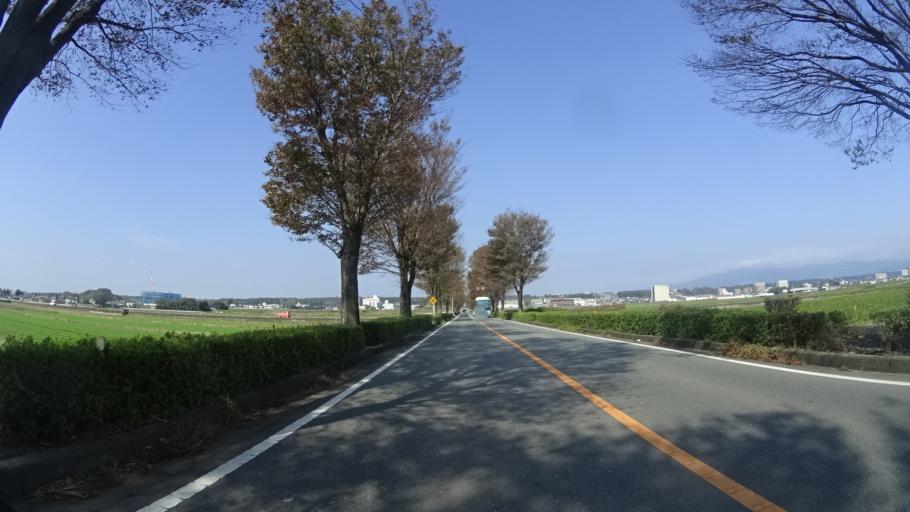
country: JP
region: Kumamoto
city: Ozu
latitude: 32.8676
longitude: 130.8552
